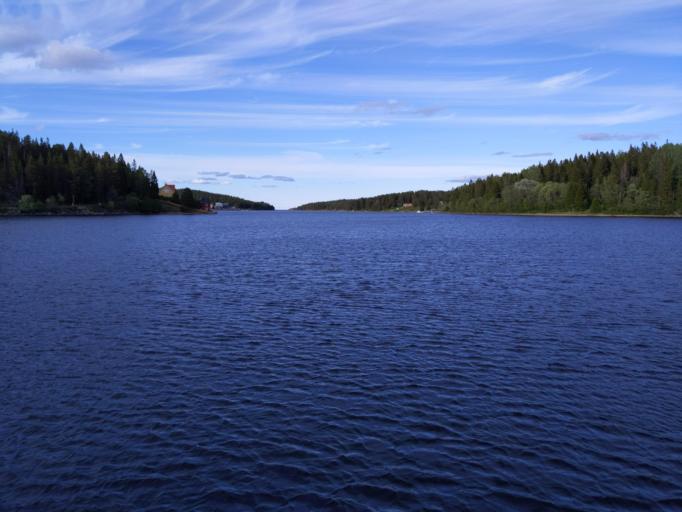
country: SE
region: Vaesternorrland
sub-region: OErnskoeldsviks Kommun
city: Kopmanholmen
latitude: 63.0151
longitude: 18.6377
